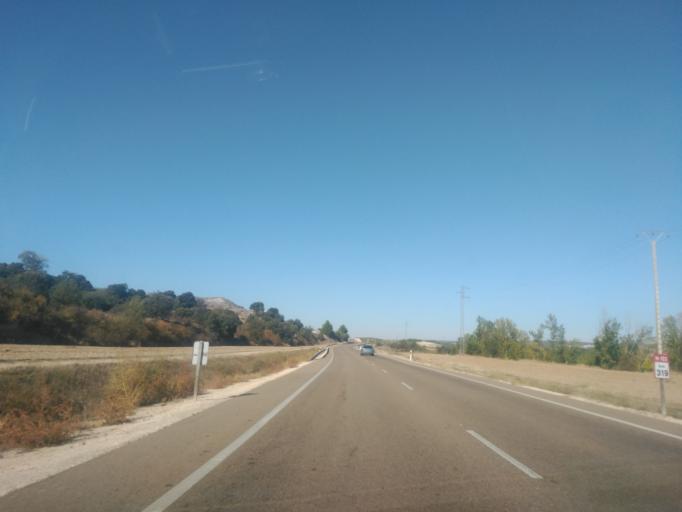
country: ES
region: Castille and Leon
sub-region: Provincia de Valladolid
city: Quintanilla de Arriba
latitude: 41.6226
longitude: -4.2493
